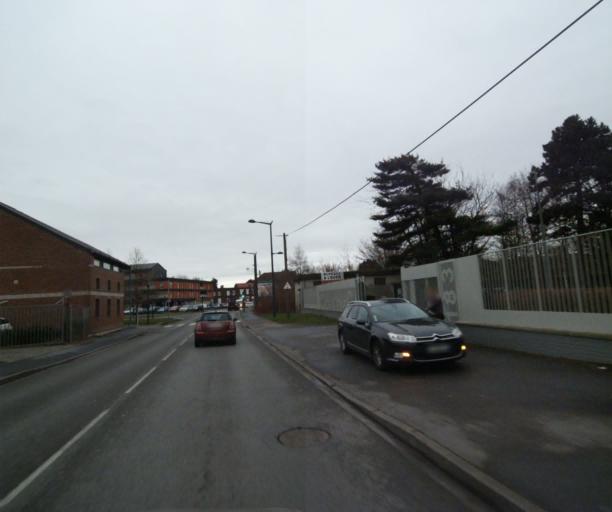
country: FR
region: Nord-Pas-de-Calais
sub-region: Departement du Nord
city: Petite-Foret
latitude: 50.3633
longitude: 3.4905
